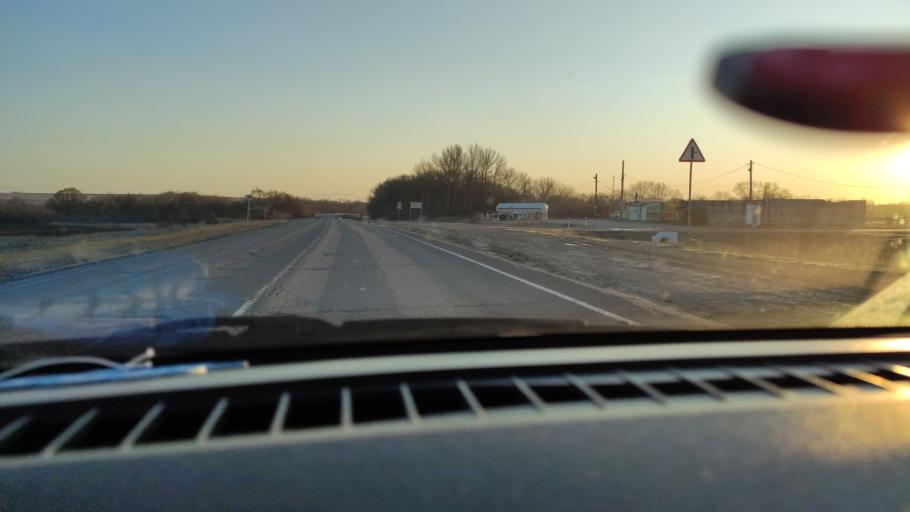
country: RU
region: Saratov
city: Sinodskoye
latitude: 51.9735
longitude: 46.6455
